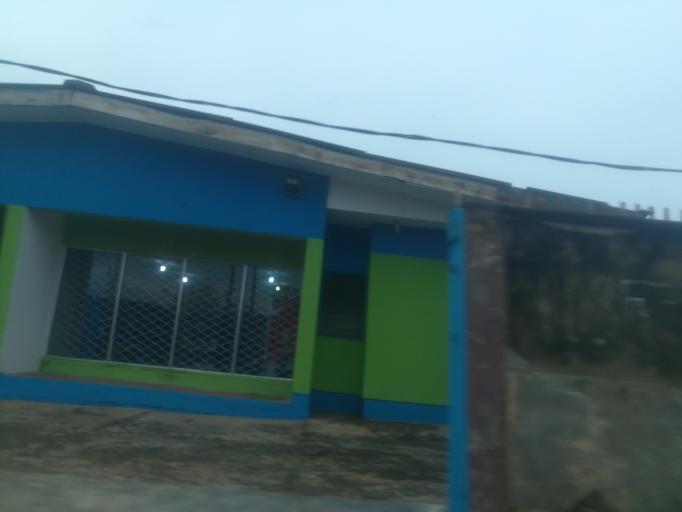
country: NG
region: Oyo
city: Egbeda
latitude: 7.3972
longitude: 3.9786
